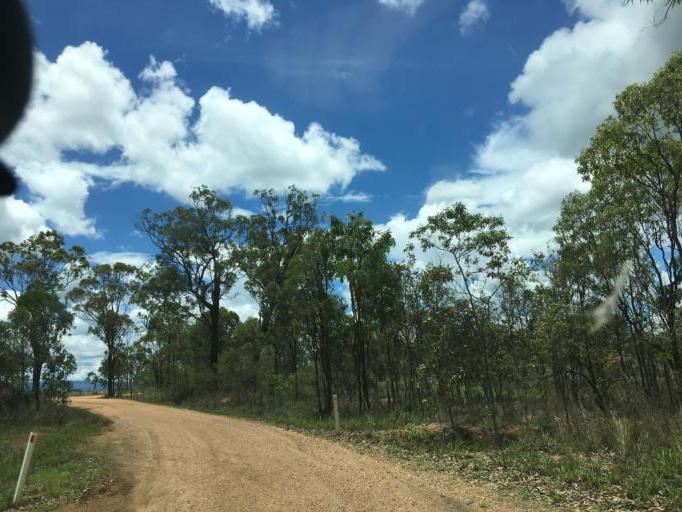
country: AU
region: Queensland
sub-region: Tablelands
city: Mareeba
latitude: -16.9930
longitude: 145.5206
